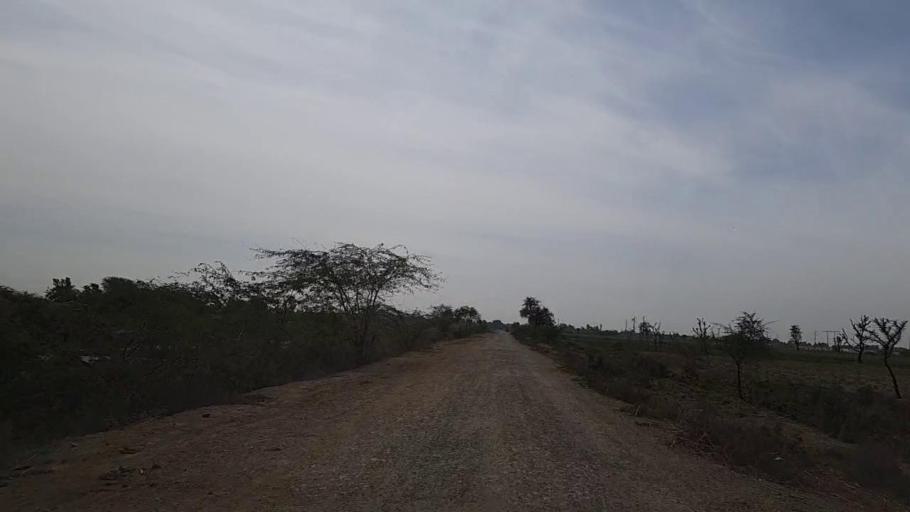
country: PK
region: Sindh
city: Samaro
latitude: 25.2985
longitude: 69.4189
